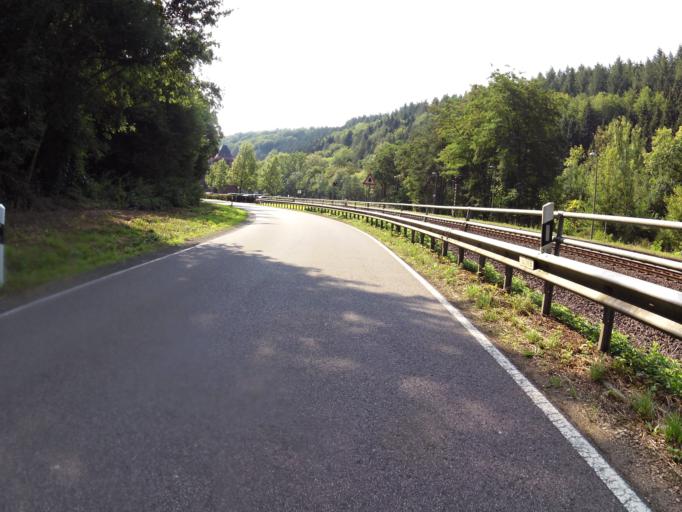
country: DE
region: Rheinland-Pfalz
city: Speicher
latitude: 49.9305
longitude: 6.6150
